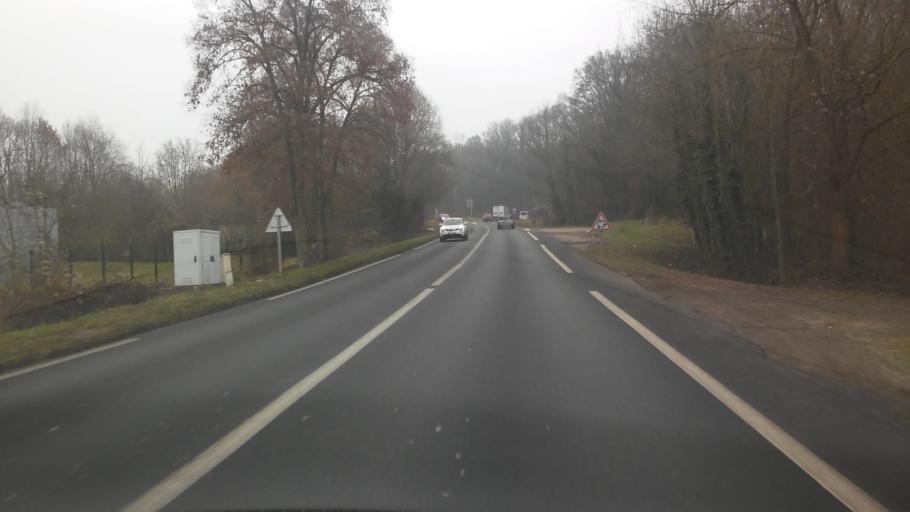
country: FR
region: Lorraine
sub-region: Departement de la Moselle
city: Augny
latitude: 49.0745
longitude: 6.1073
